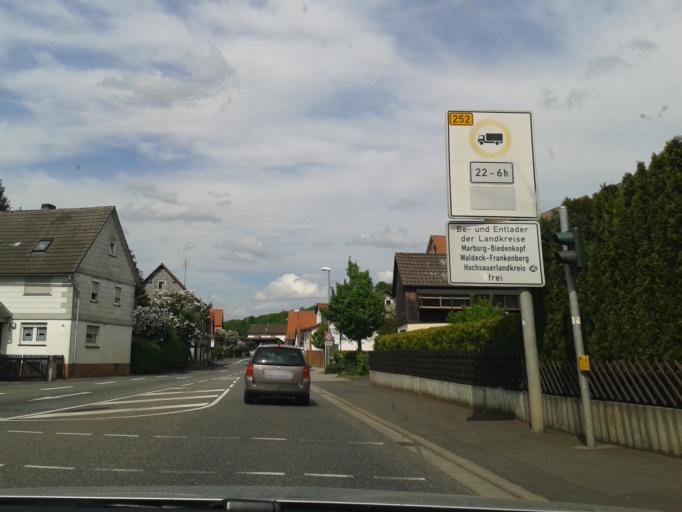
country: DE
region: Hesse
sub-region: Regierungsbezirk Giessen
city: Munchhausen
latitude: 50.9616
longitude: 8.7168
